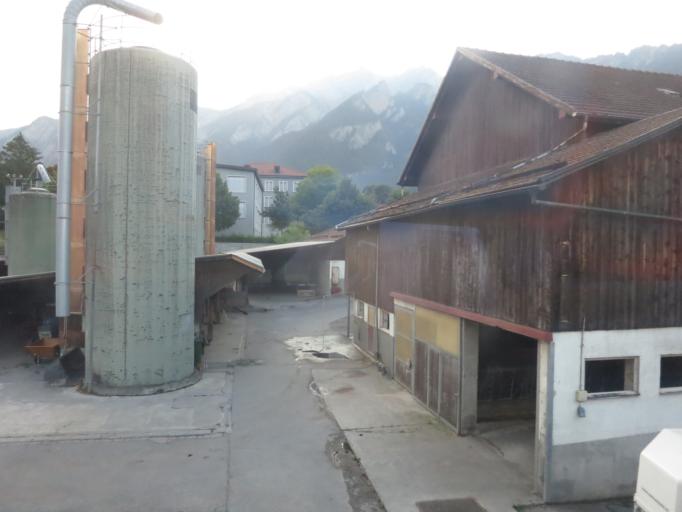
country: CH
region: Grisons
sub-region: Plessur District
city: Chur
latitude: 46.8689
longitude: 9.5324
